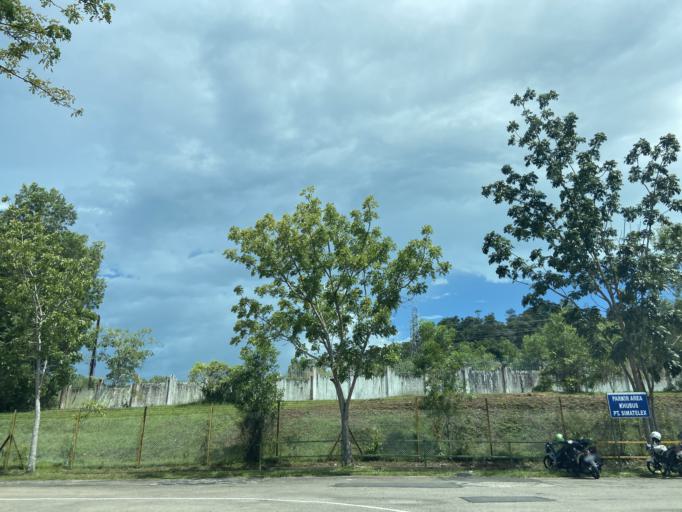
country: SG
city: Singapore
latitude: 1.0527
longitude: 104.0400
